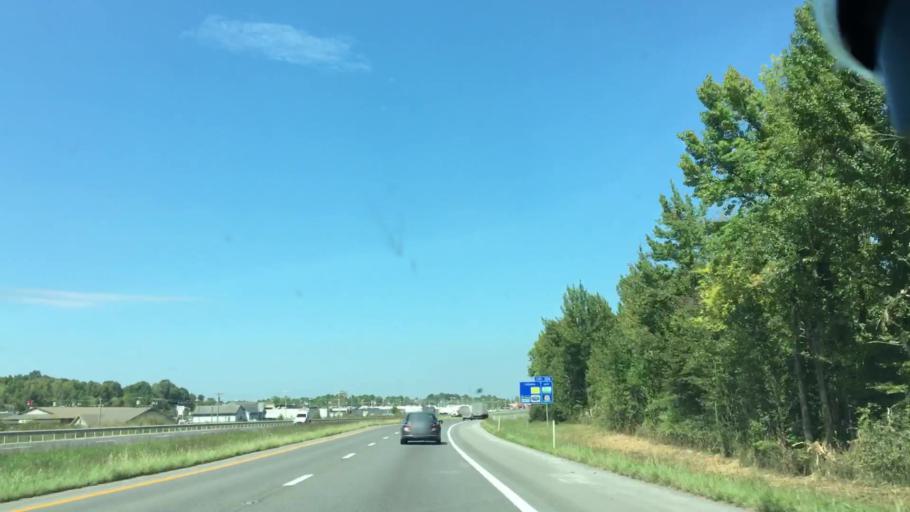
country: US
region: Kentucky
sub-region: Hopkins County
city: Madisonville
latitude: 37.3195
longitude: -87.4746
